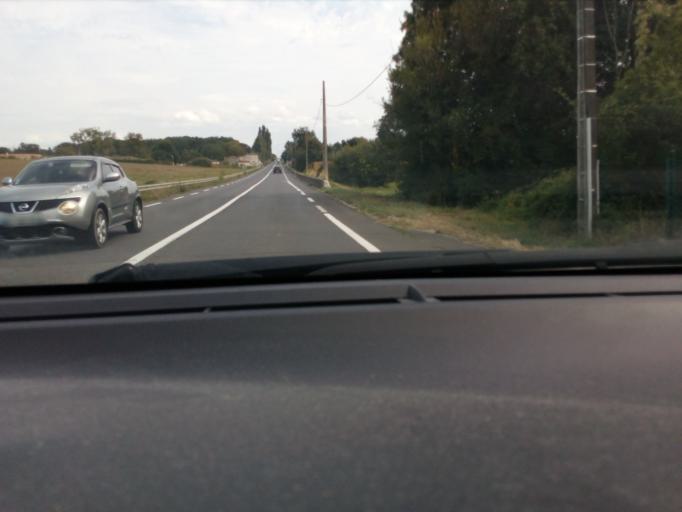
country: FR
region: Poitou-Charentes
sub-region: Departement de la Charente
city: Fleac
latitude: 45.6759
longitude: 0.0888
